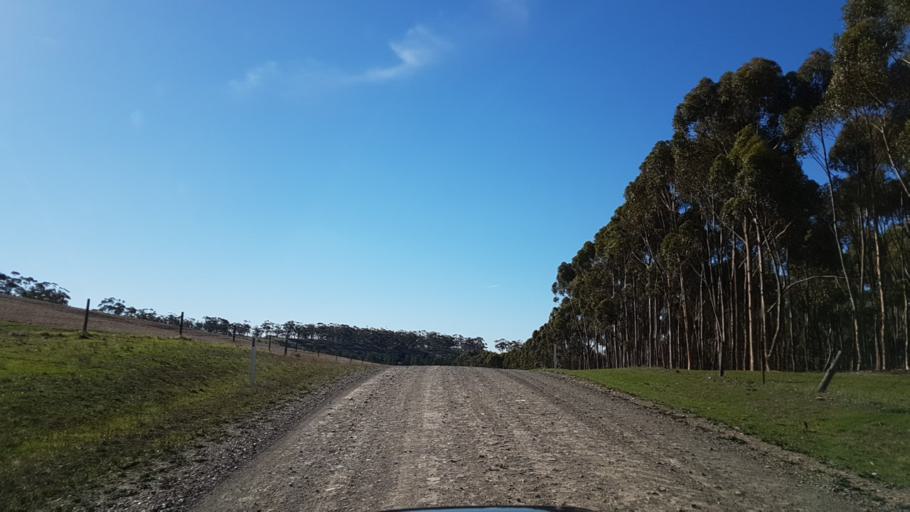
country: AU
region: South Australia
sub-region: Northern Areas
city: Jamestown
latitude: -33.2815
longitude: 138.5595
